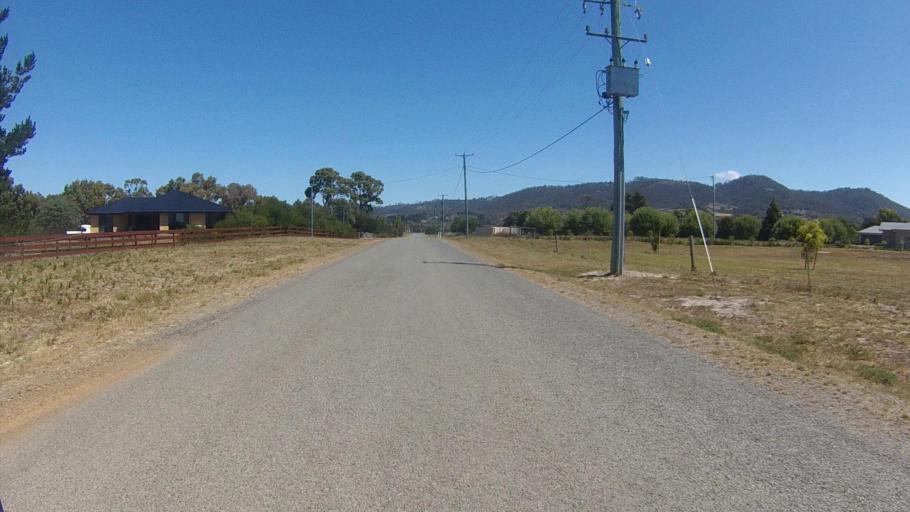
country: AU
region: Tasmania
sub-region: Clarence
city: Seven Mile Beach
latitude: -42.8492
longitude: 147.4934
